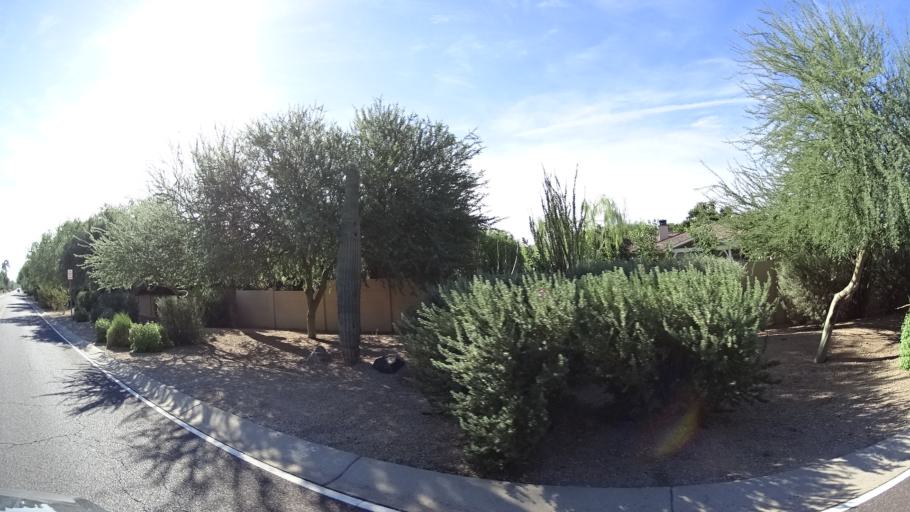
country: US
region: Arizona
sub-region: Maricopa County
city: Paradise Valley
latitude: 33.5166
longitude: -111.9376
